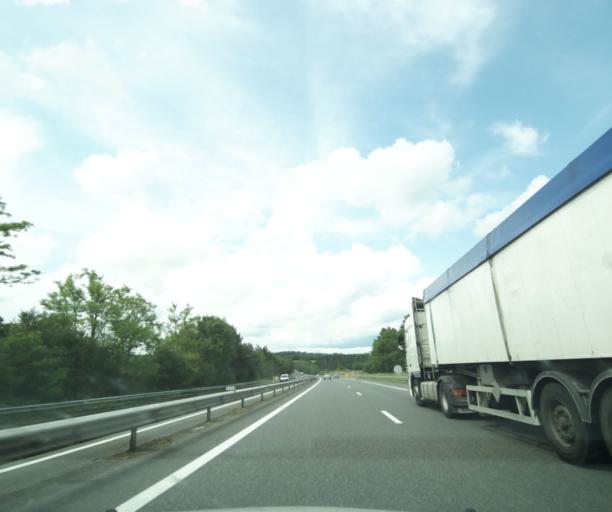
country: FR
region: Auvergne
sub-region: Departement de l'Allier
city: Bellenaves
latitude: 46.2303
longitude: 3.0998
